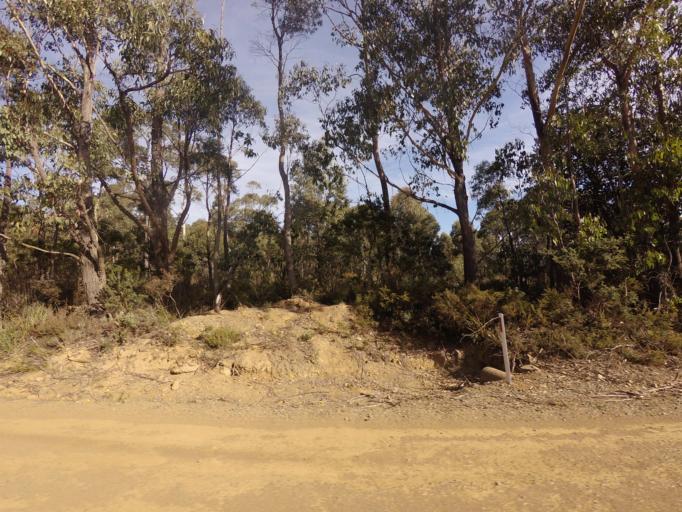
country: AU
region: Tasmania
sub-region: Sorell
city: Sorell
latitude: -42.4991
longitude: 147.5330
